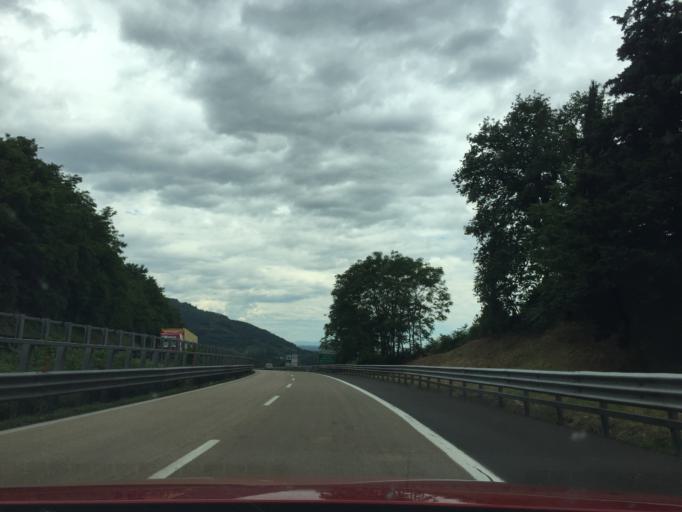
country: IT
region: Tuscany
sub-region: Provincia di Pistoia
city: Serravalle Pistoiese
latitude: 43.9008
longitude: 10.8281
